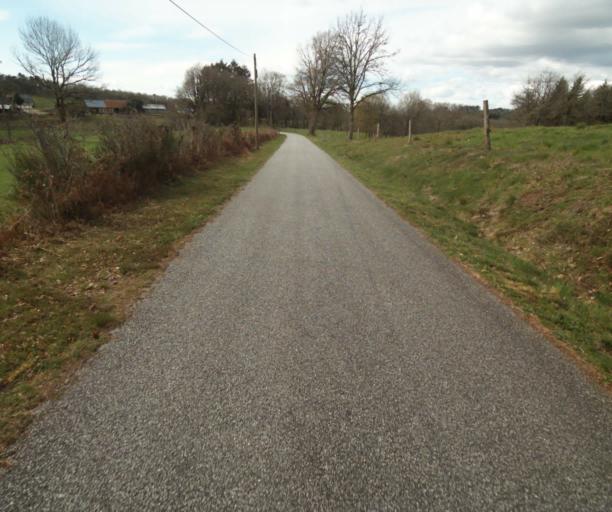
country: FR
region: Limousin
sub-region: Departement de la Correze
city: Correze
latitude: 45.3888
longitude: 1.8972
